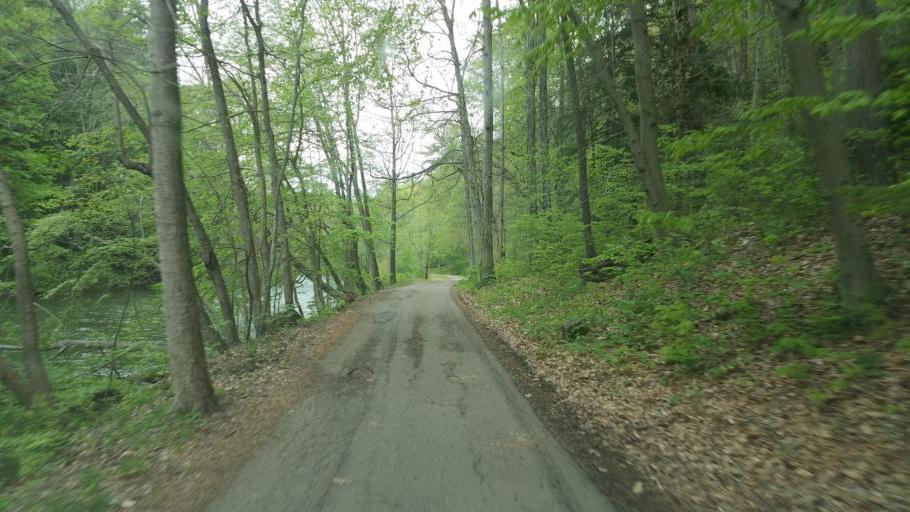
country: US
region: Ohio
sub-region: Ashland County
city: Loudonville
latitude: 40.6112
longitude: -82.3071
